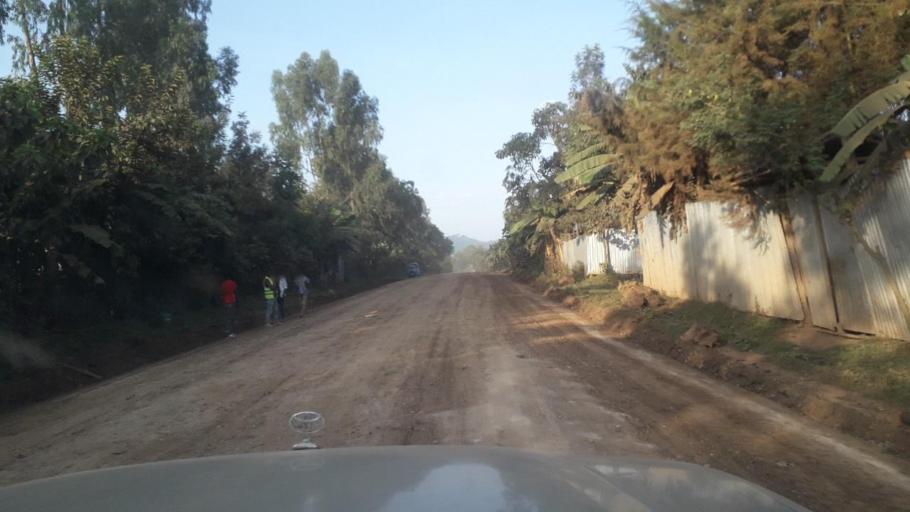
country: ET
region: Oromiya
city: Jima
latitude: 7.6307
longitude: 36.8302
